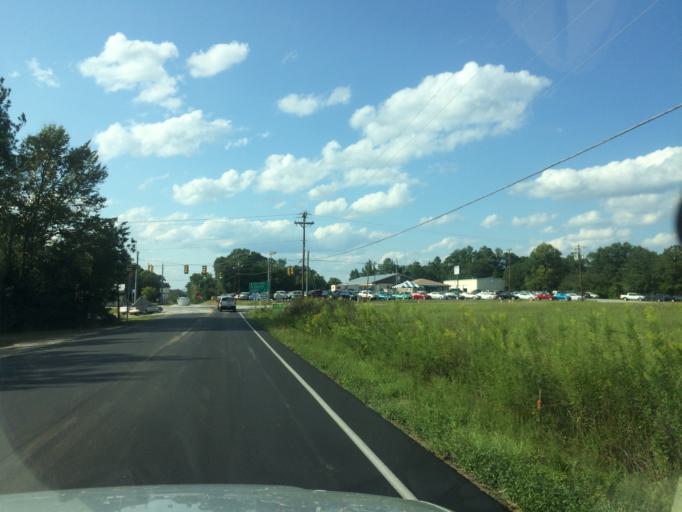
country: US
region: South Carolina
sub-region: Greenwood County
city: Ware Shoals
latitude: 34.5204
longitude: -82.1887
